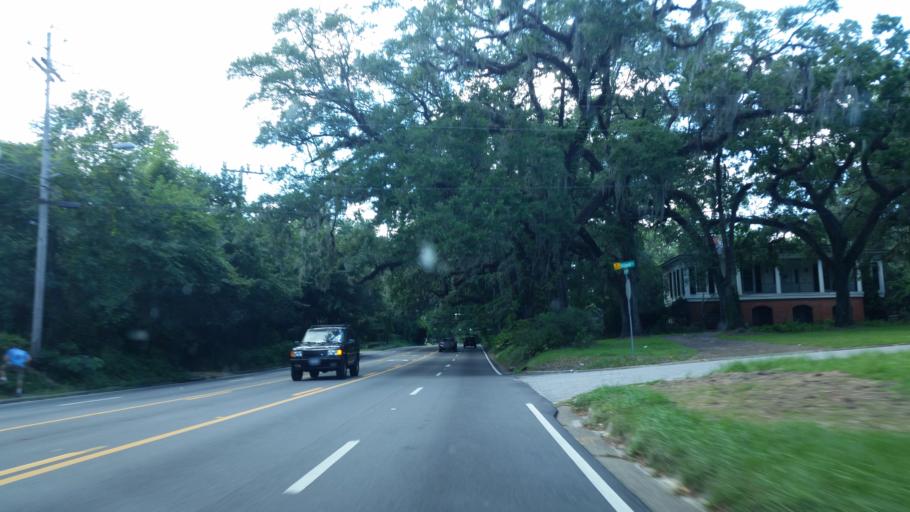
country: US
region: Alabama
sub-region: Mobile County
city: Mobile
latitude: 30.6765
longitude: -88.0995
